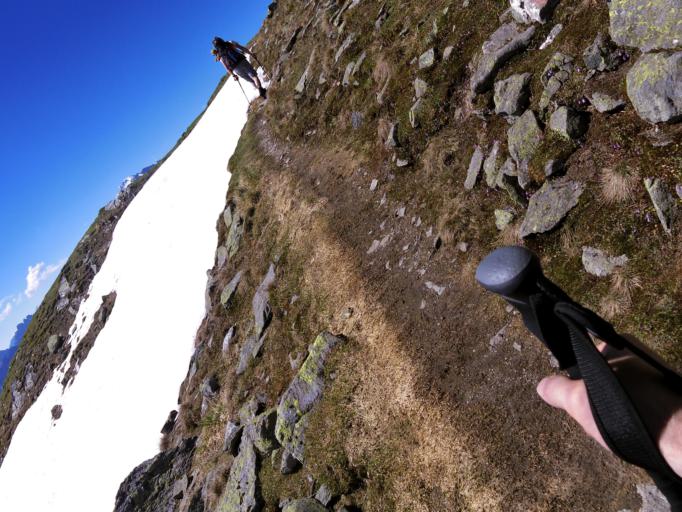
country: AT
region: Tyrol
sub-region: Politischer Bezirk Innsbruck Land
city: Neustift im Stubaital
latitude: 47.1389
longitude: 11.2599
